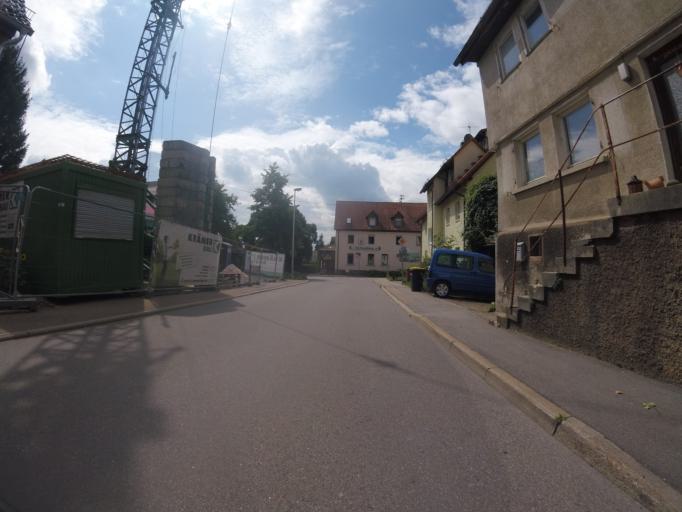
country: DE
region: Baden-Wuerttemberg
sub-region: Regierungsbezirk Stuttgart
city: Winnenden
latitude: 48.8337
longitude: 9.4221
